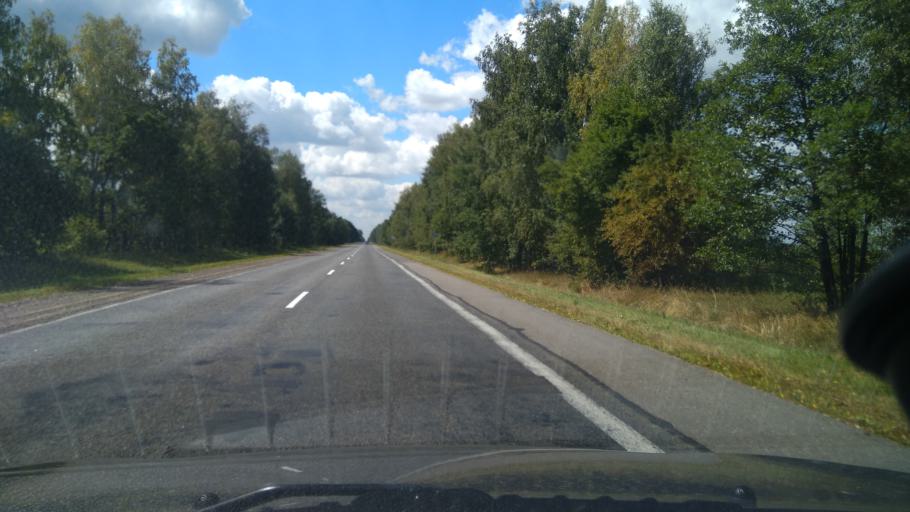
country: BY
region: Brest
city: Ivatsevichy
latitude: 52.6847
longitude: 25.2878
